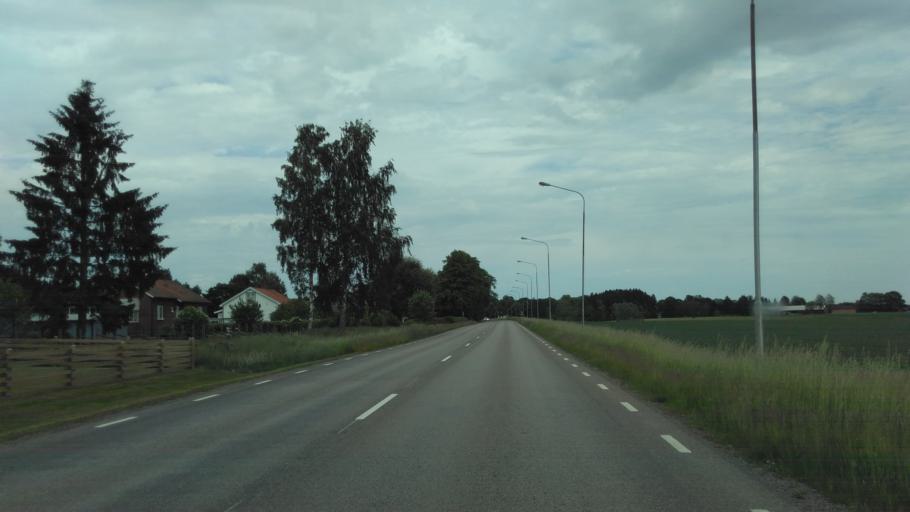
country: SE
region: Vaestra Goetaland
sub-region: Lidkopings Kommun
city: Lidkoping
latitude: 58.4338
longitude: 13.1599
